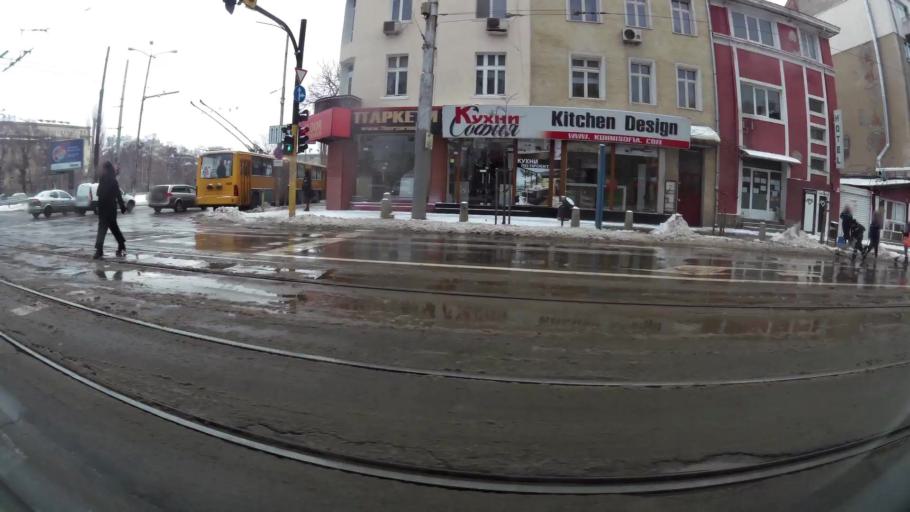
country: BG
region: Sofia-Capital
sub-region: Stolichna Obshtina
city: Sofia
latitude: 42.7050
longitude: 23.3175
